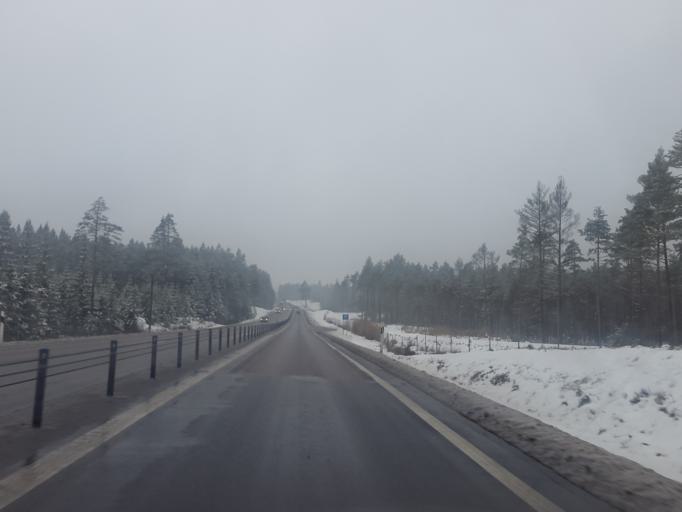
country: SE
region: Joenkoeping
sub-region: Jonkopings Kommun
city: Taberg
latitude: 57.7589
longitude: 14.0021
